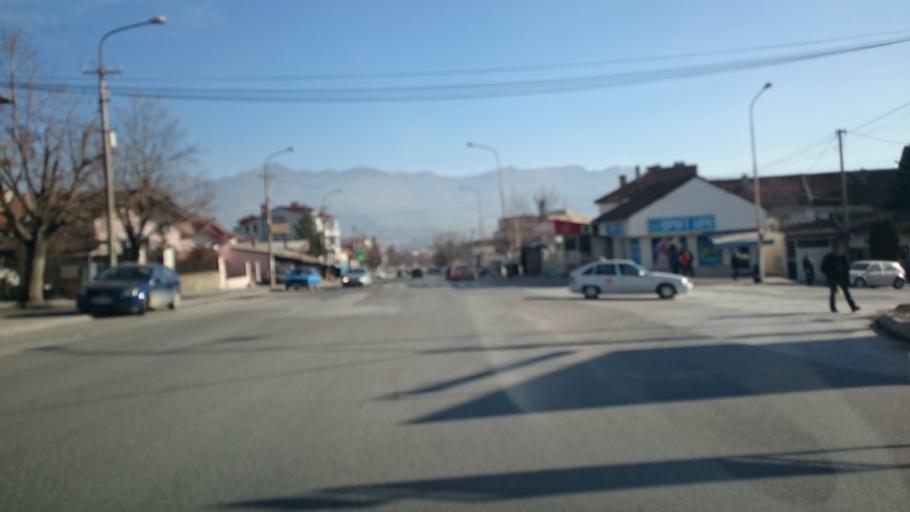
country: MK
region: Prilep
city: Markov Grad
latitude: 41.3532
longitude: 21.5436
